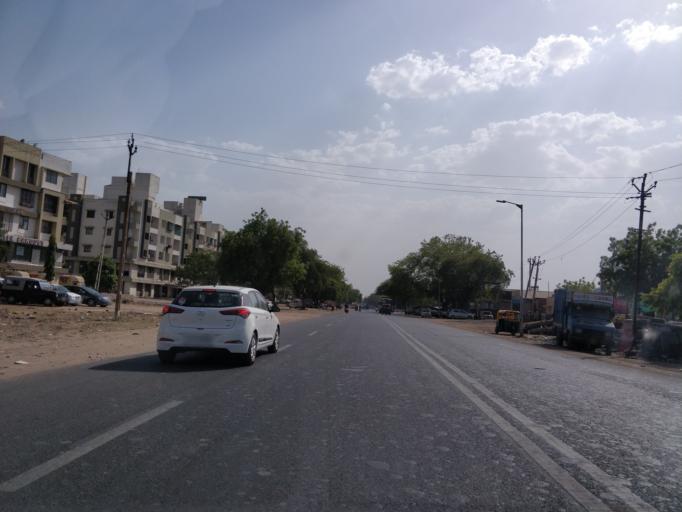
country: IN
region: Gujarat
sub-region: Ahmadabad
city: Naroda
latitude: 23.0802
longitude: 72.6698
